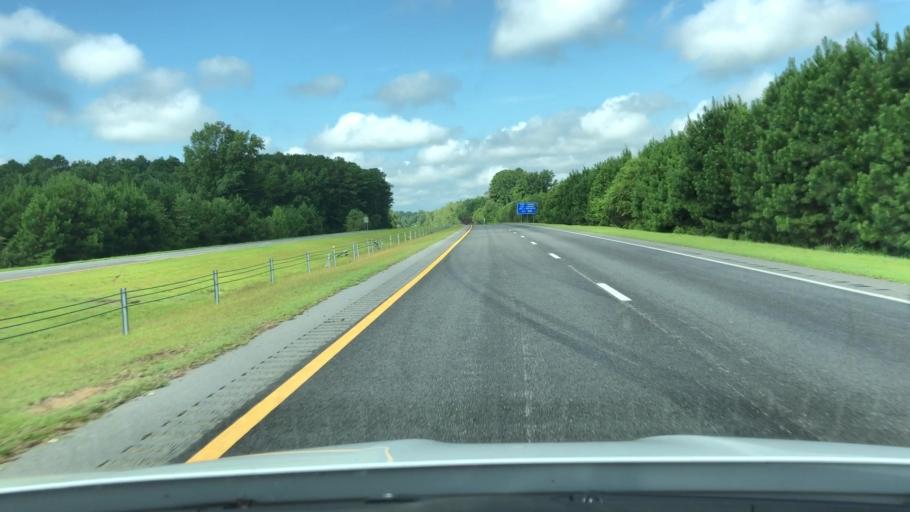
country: US
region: North Carolina
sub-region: Bertie County
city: Windsor
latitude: 36.0169
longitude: -76.9361
